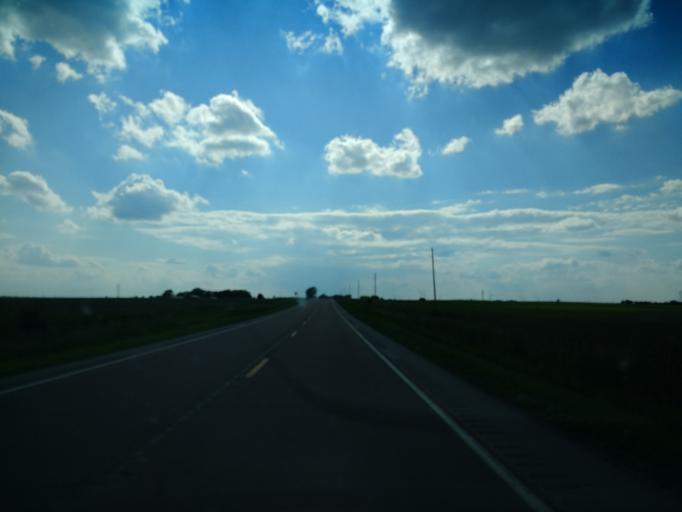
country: US
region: Iowa
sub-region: Clay County
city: Spencer
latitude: 43.1836
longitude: -95.2321
